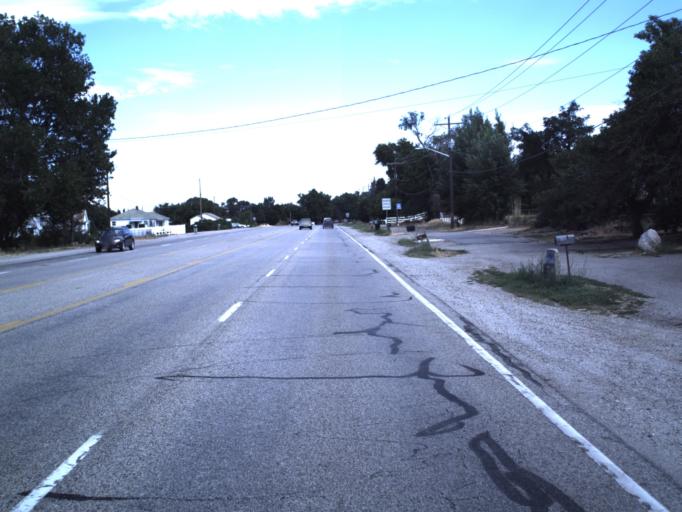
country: US
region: Utah
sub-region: Box Elder County
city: Willard
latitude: 41.4014
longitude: -112.0353
